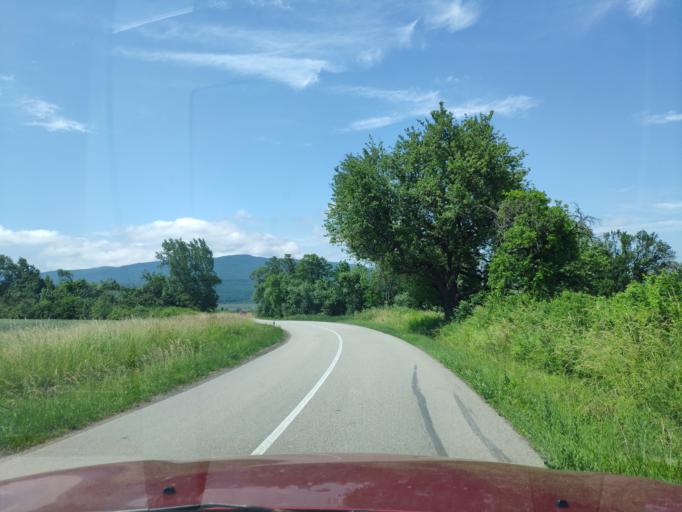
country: SK
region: Kosicky
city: Secovce
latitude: 48.7407
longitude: 21.6486
